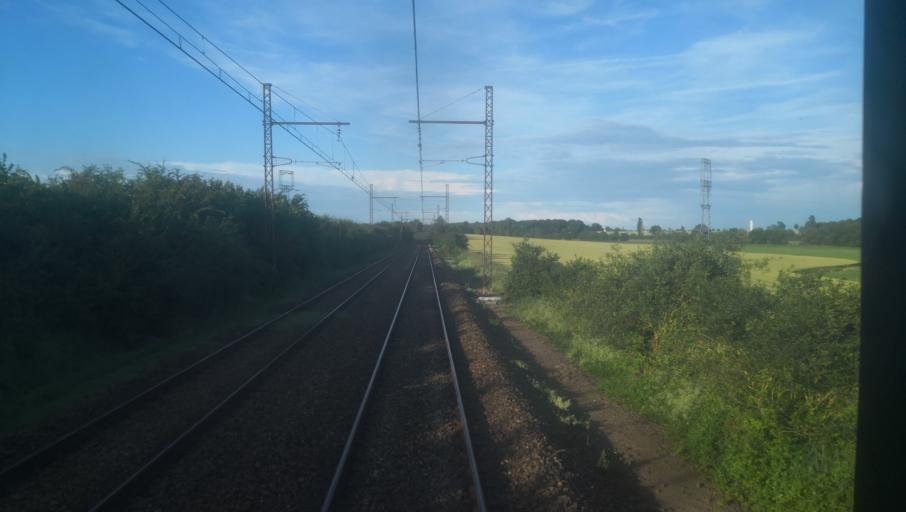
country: FR
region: Centre
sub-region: Departement de l'Indre
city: Neuvy-Pailloux
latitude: 46.8948
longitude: 1.8897
